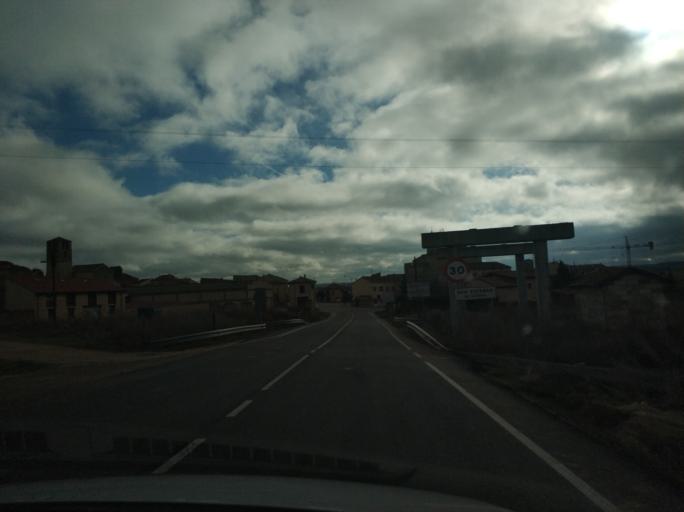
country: ES
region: Castille and Leon
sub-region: Provincia de Soria
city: San Esteban de Gormaz
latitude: 41.5773
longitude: -3.2085
